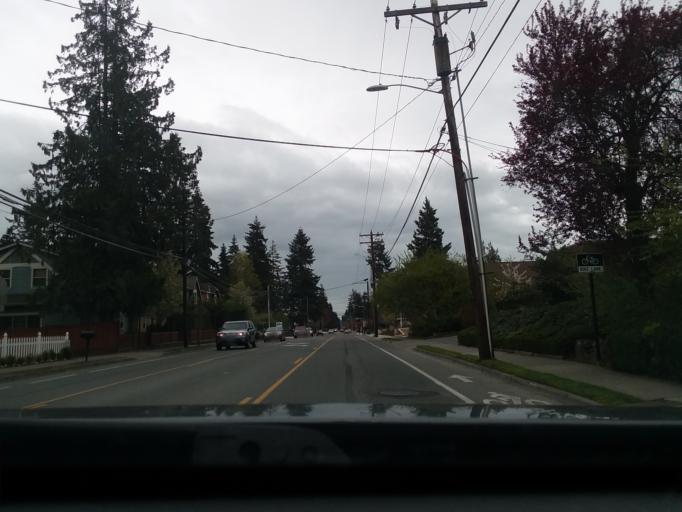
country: US
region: Washington
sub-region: Snohomish County
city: Lynnwood
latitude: 47.8096
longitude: -122.3358
